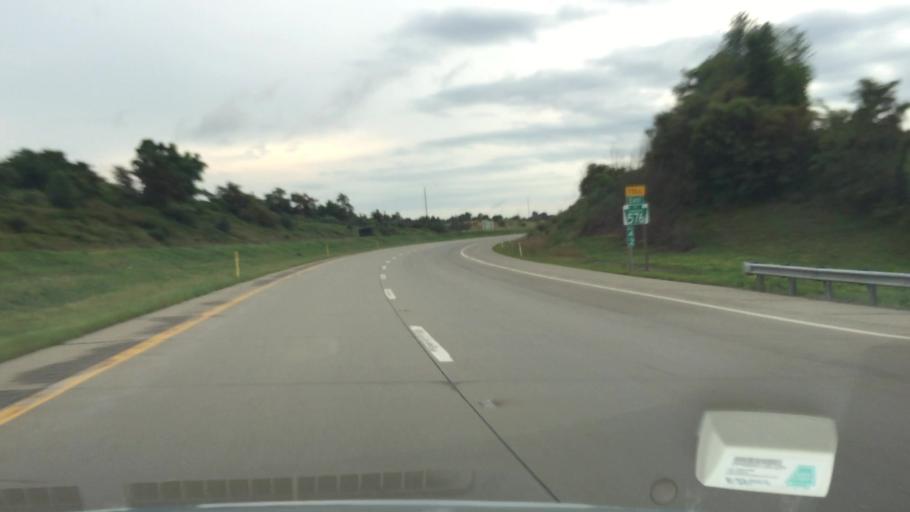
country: US
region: Pennsylvania
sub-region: Allegheny County
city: Imperial
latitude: 40.4417
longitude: -80.3108
